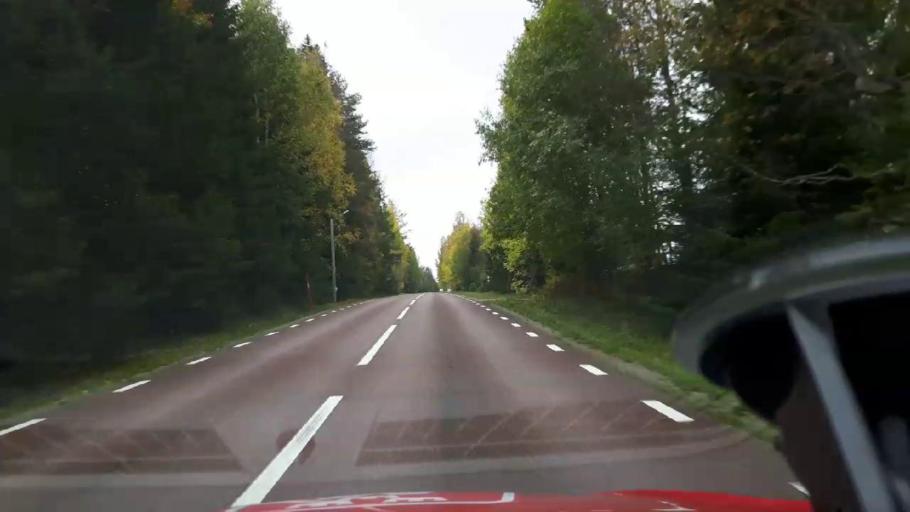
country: SE
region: Jaemtland
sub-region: Harjedalens Kommun
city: Sveg
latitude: 62.1991
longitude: 14.8545
